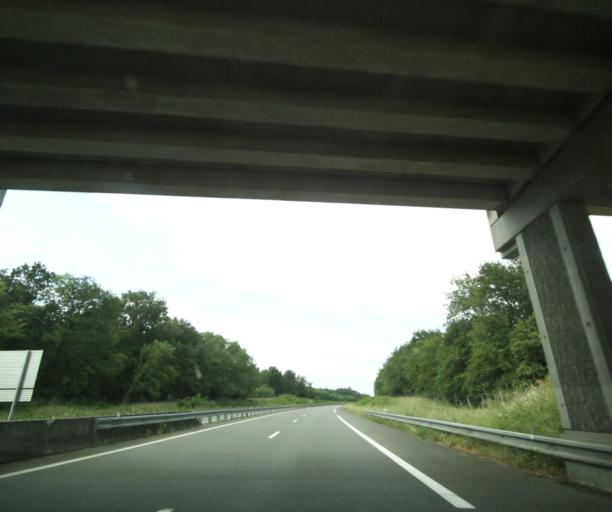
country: FR
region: Pays de la Loire
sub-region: Departement de Maine-et-Loire
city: Brion
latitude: 47.4428
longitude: -0.1758
